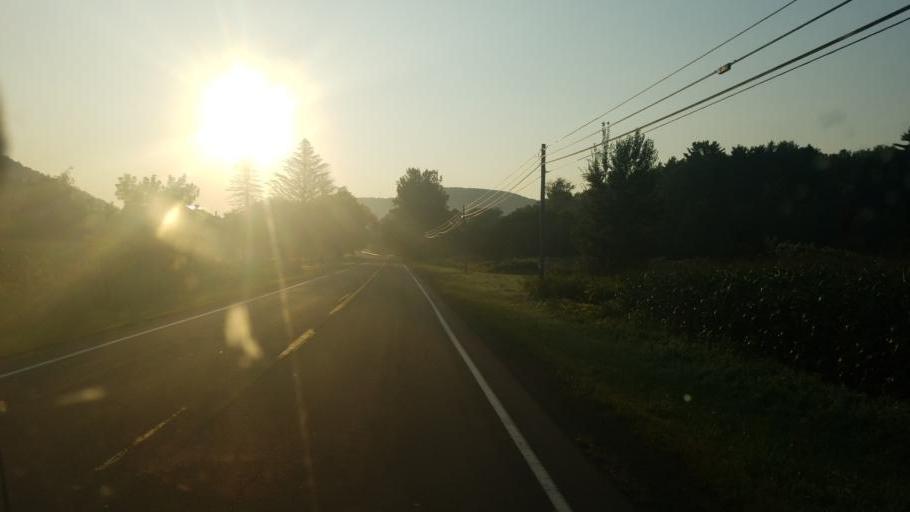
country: US
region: Pennsylvania
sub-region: Tioga County
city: Westfield
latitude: 41.9130
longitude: -77.5967
